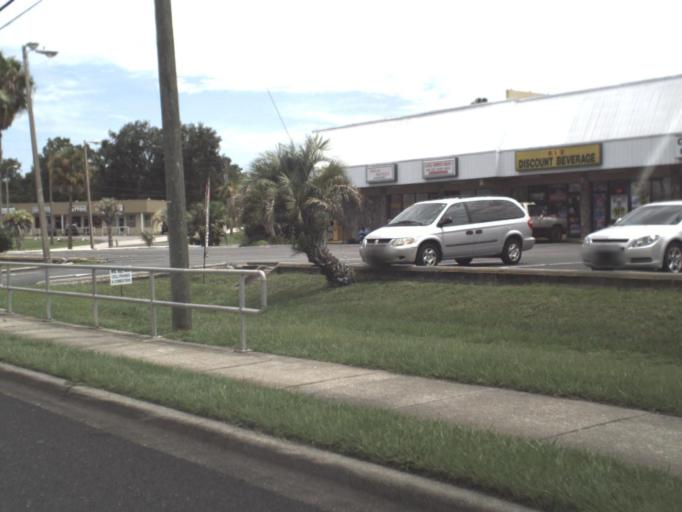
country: US
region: Florida
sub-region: Citrus County
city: Inverness Highlands North
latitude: 28.8471
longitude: -82.3713
